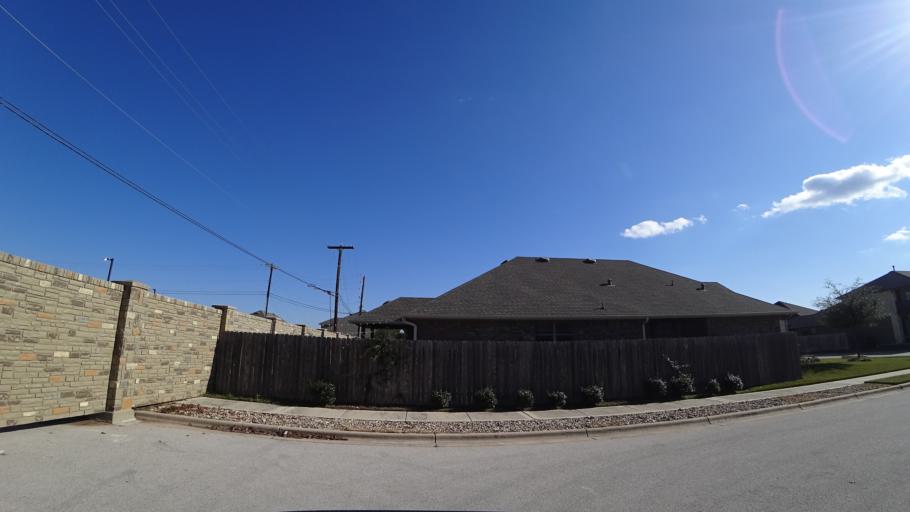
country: US
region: Texas
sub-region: Williamson County
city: Brushy Creek
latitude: 30.4907
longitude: -97.7263
